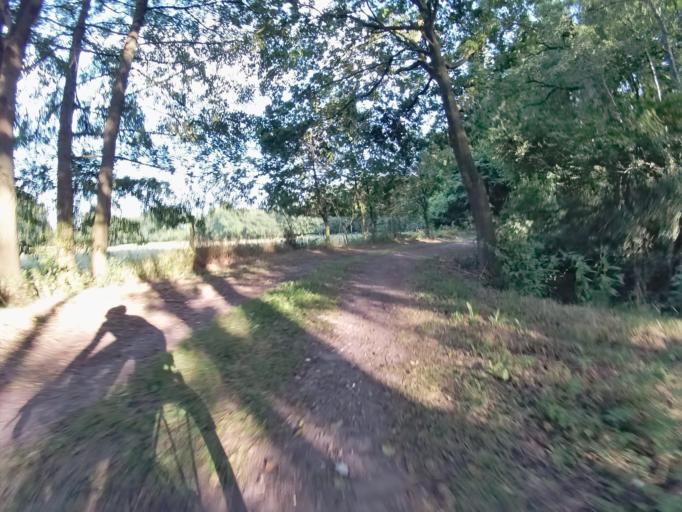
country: DE
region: North Rhine-Westphalia
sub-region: Regierungsbezirk Munster
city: Westerkappeln
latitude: 52.3185
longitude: 7.8393
